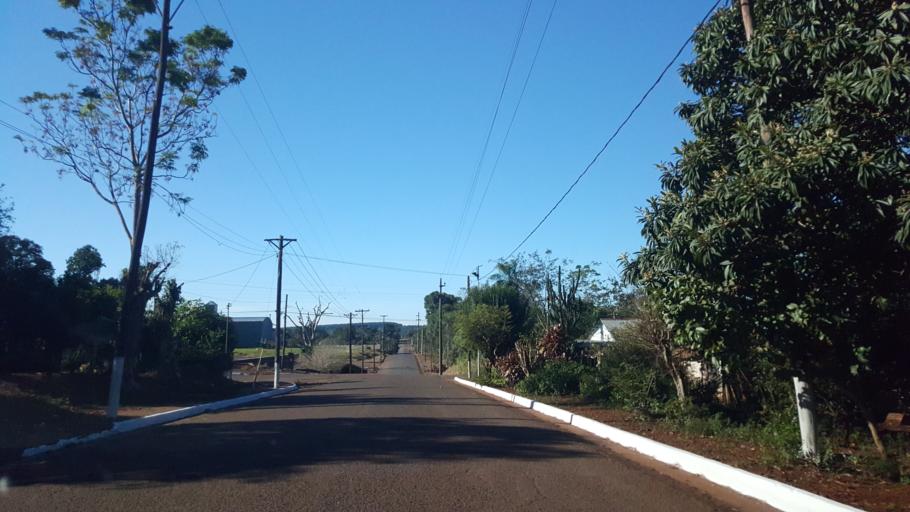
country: AR
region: Misiones
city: Gobernador Roca
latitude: -27.1864
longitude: -55.4632
